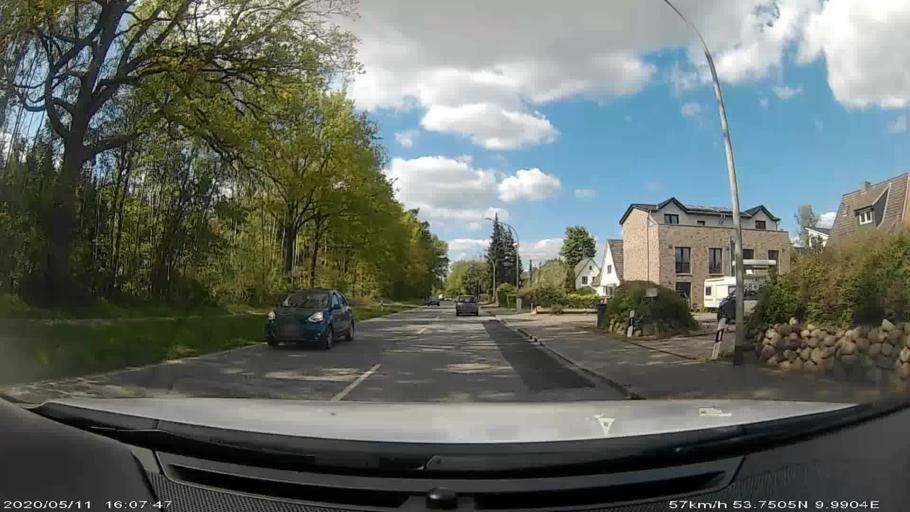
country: DE
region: Schleswig-Holstein
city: Henstedt-Ulzburg
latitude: 53.7540
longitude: 9.9931
